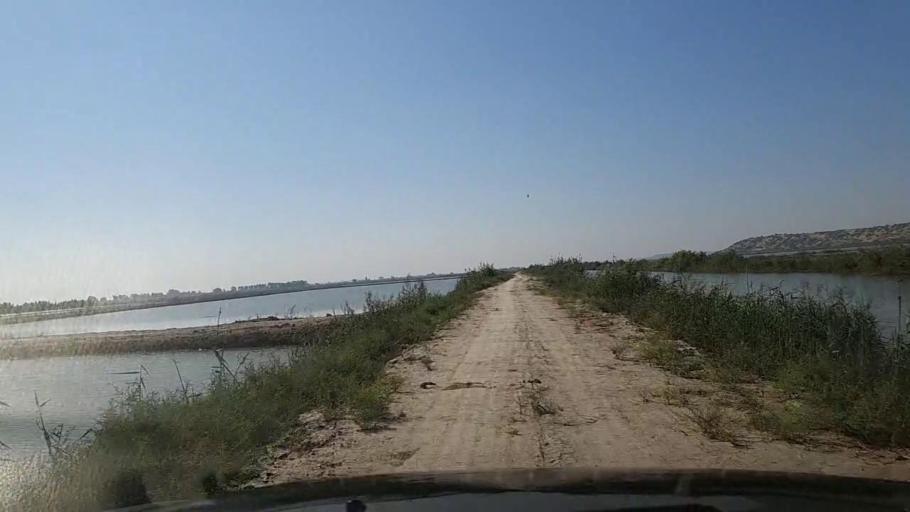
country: PK
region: Sindh
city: Thatta
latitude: 24.6816
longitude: 67.8909
